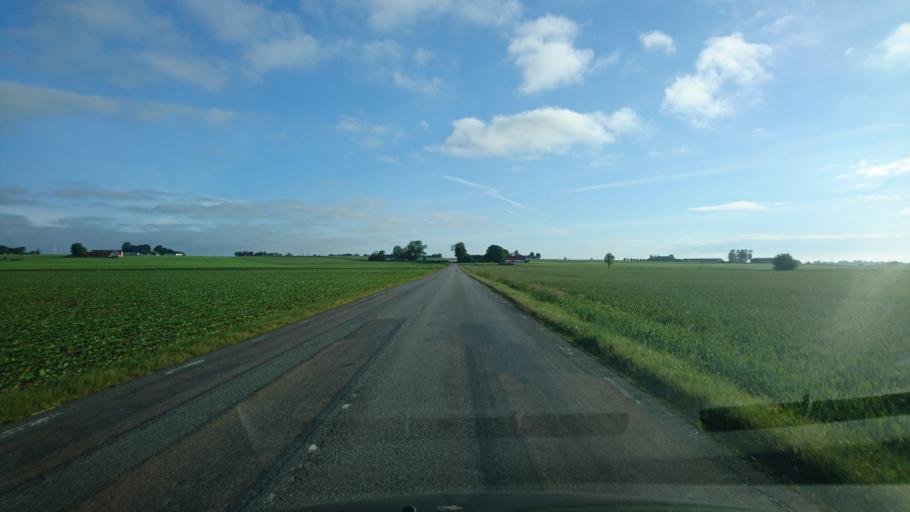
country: SE
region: Skane
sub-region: Tomelilla Kommun
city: Tomelilla
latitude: 55.4744
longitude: 14.0989
